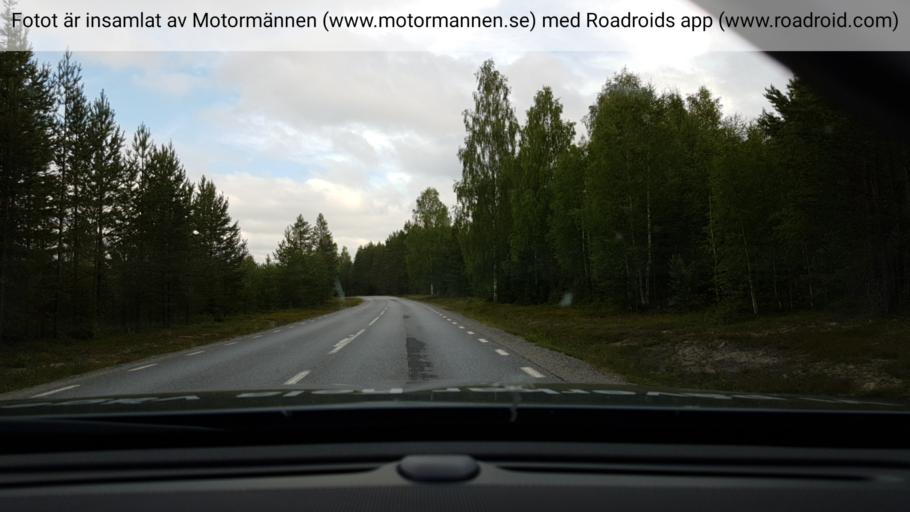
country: SE
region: Vaesterbotten
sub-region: Vindelns Kommun
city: Vindeln
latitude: 64.2726
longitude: 19.6340
